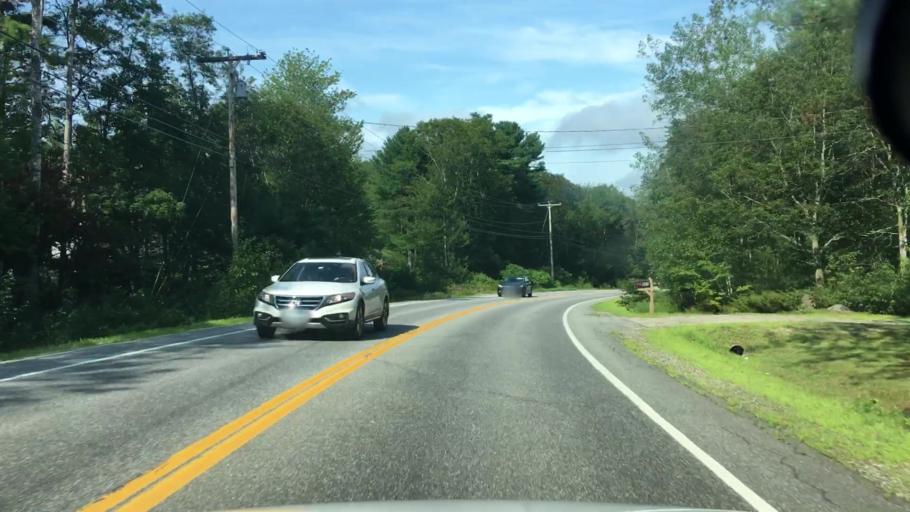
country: US
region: Maine
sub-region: Cumberland County
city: Harpswell Center
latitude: 43.8129
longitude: -69.9276
